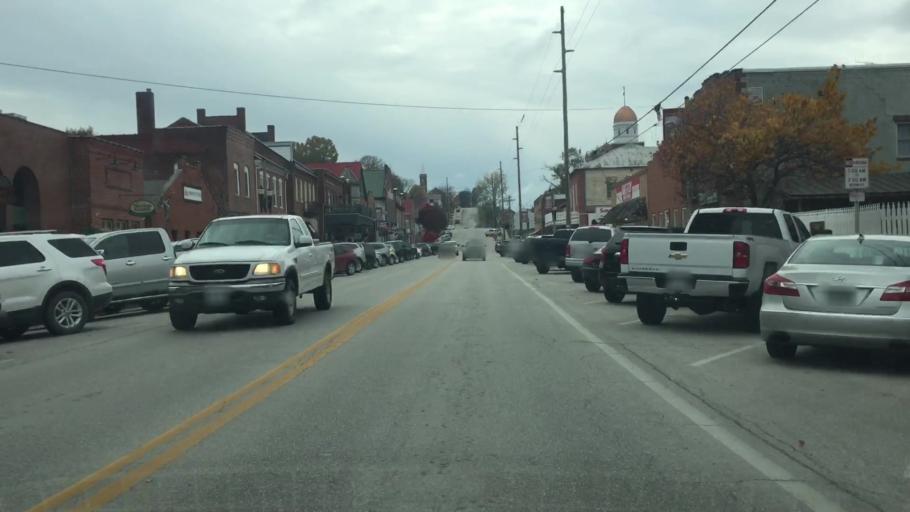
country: US
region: Missouri
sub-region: Gasconade County
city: Hermann
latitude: 38.7067
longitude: -91.4330
